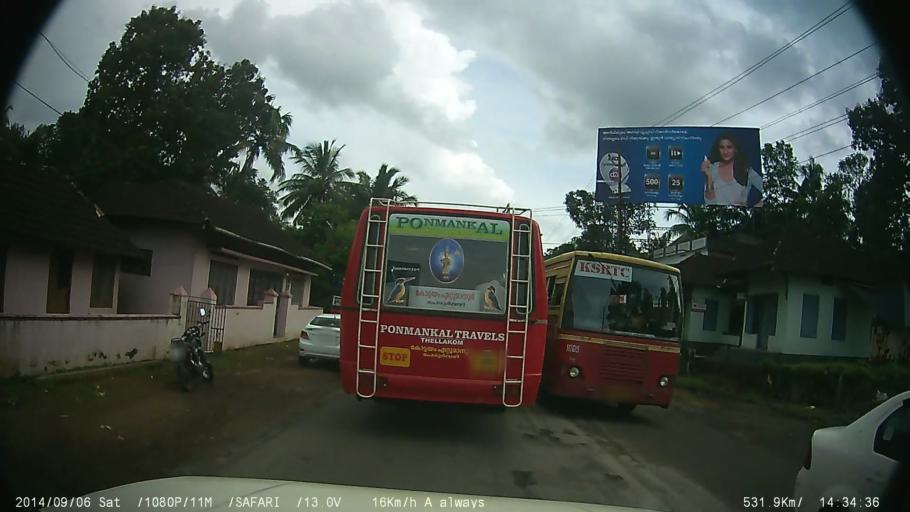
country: IN
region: Kerala
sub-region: Kottayam
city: Kottayam
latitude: 9.6049
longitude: 76.5321
